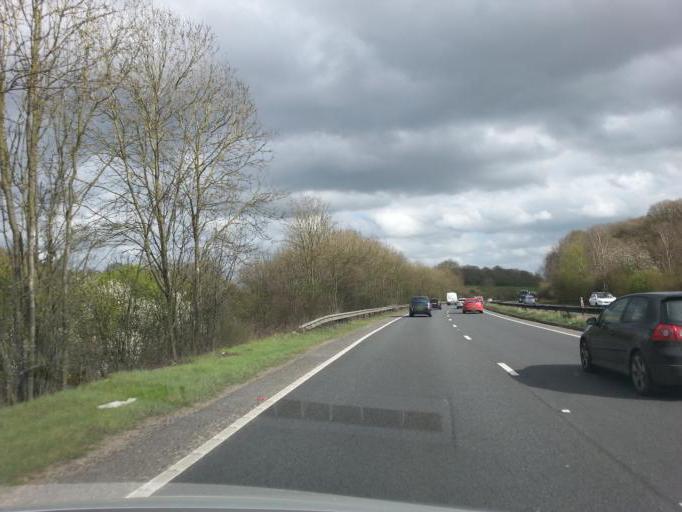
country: GB
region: England
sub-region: Hampshire
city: Andover
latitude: 51.1972
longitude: -1.4284
